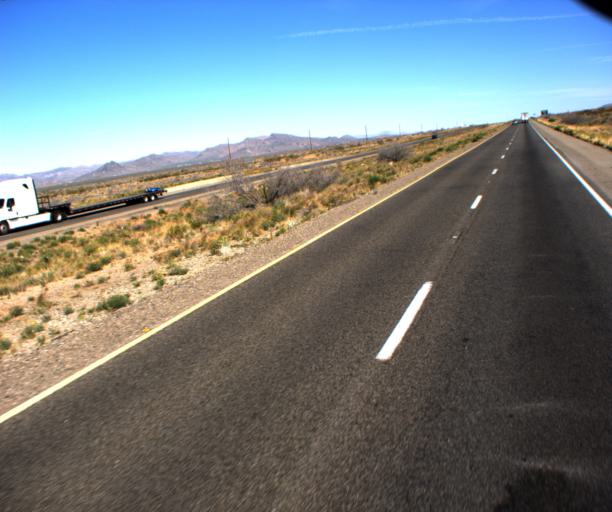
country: US
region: Arizona
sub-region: Mohave County
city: Golden Valley
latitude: 35.2835
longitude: -114.1770
